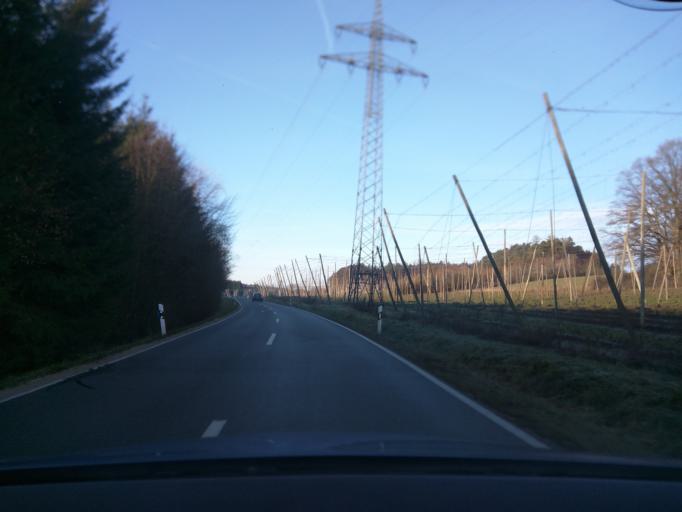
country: DE
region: Bavaria
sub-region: Upper Bavaria
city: Au in der Hallertau
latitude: 48.5673
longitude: 11.7362
